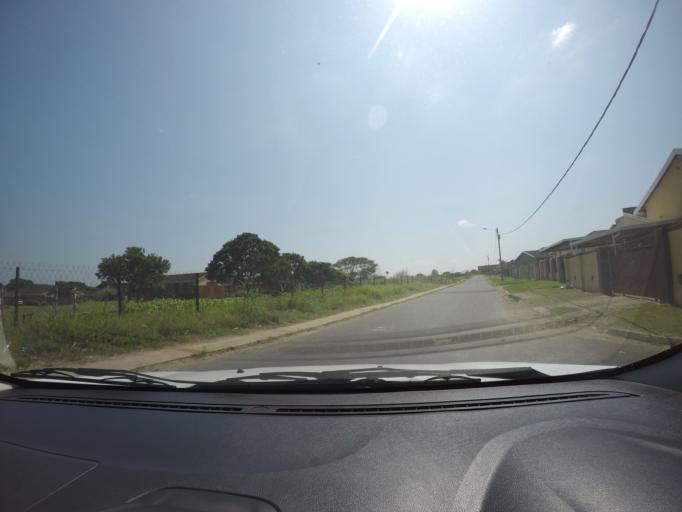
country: ZA
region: KwaZulu-Natal
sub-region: uThungulu District Municipality
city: eSikhawini
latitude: -28.8665
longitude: 31.9147
